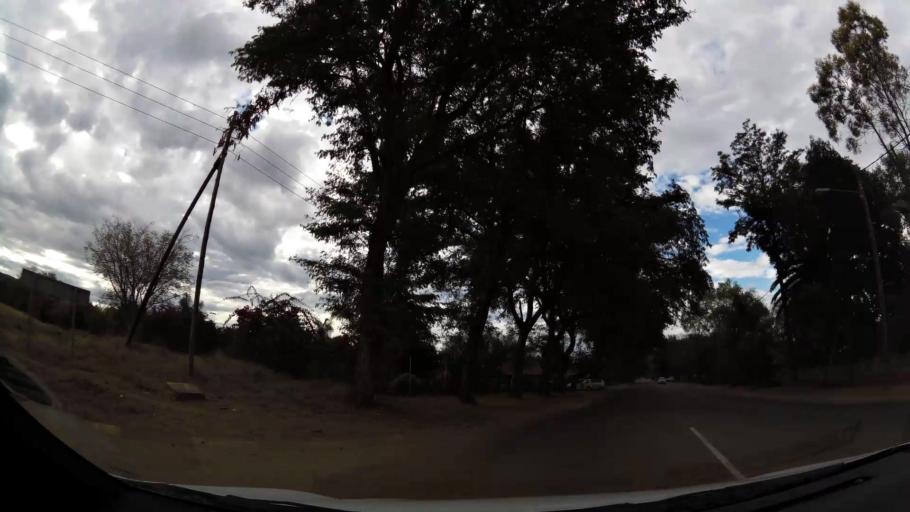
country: ZA
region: Limpopo
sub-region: Waterberg District Municipality
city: Modimolle
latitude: -24.5188
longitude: 28.7027
